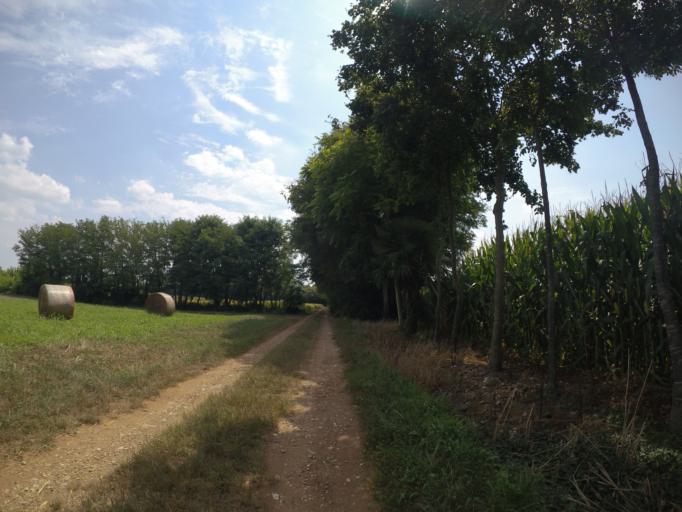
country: IT
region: Friuli Venezia Giulia
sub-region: Provincia di Udine
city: Bertiolo
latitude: 45.9588
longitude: 13.0693
